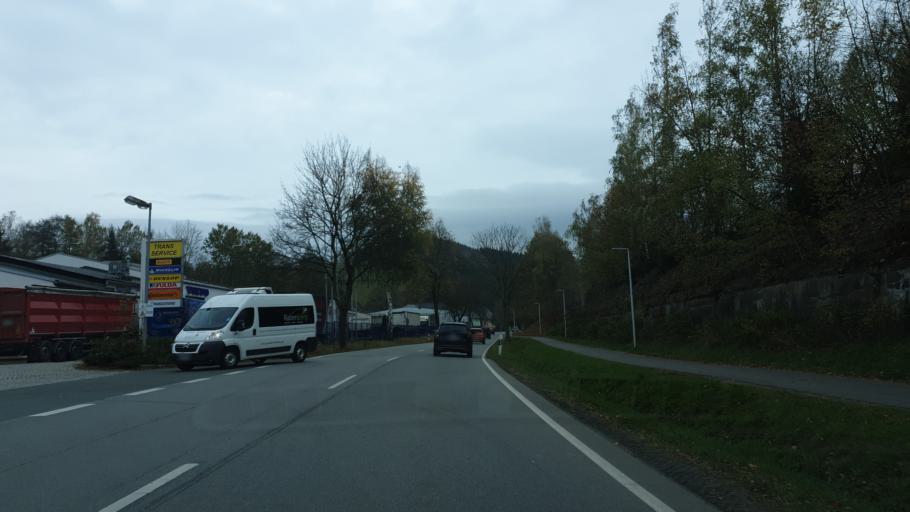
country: DE
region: Saxony
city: Schwarzenberg
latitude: 50.5240
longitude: 12.7897
